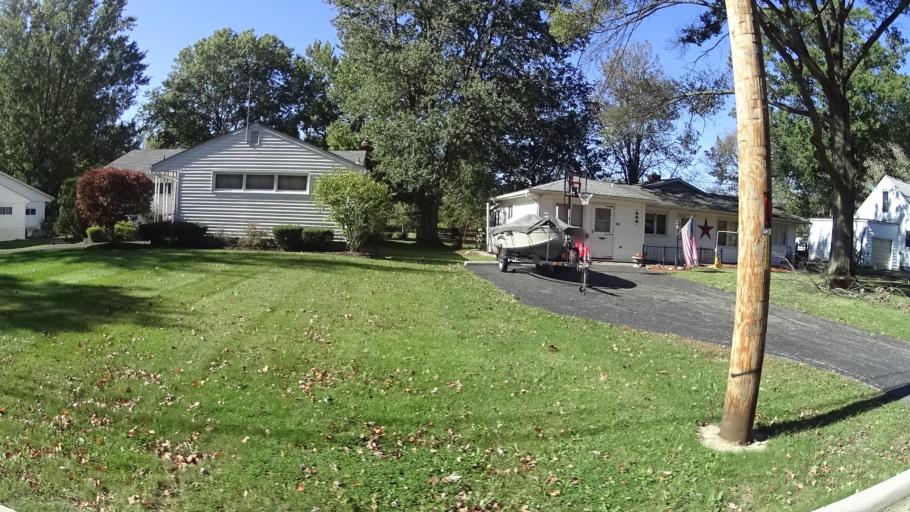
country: US
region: Ohio
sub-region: Lorain County
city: Oberlin
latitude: 41.2955
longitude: -82.2282
